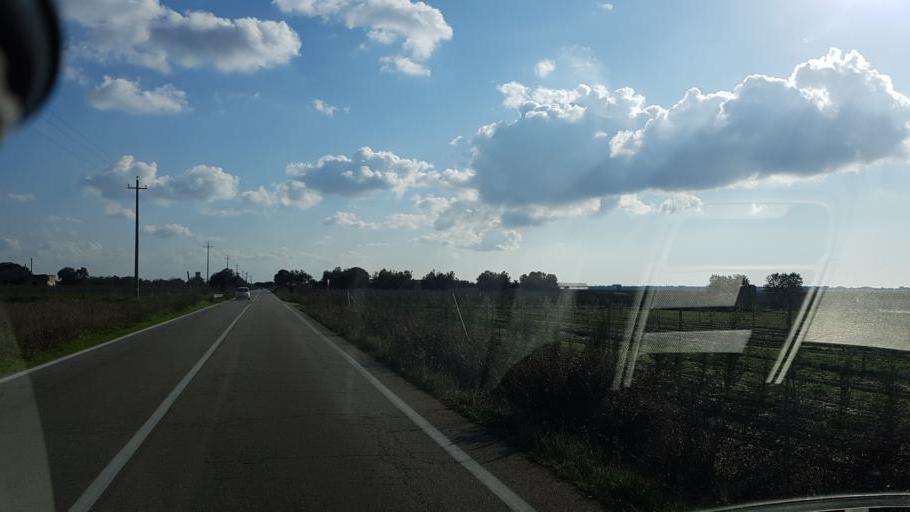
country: IT
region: Apulia
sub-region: Provincia di Lecce
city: Veglie
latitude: 40.3171
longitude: 17.9810
